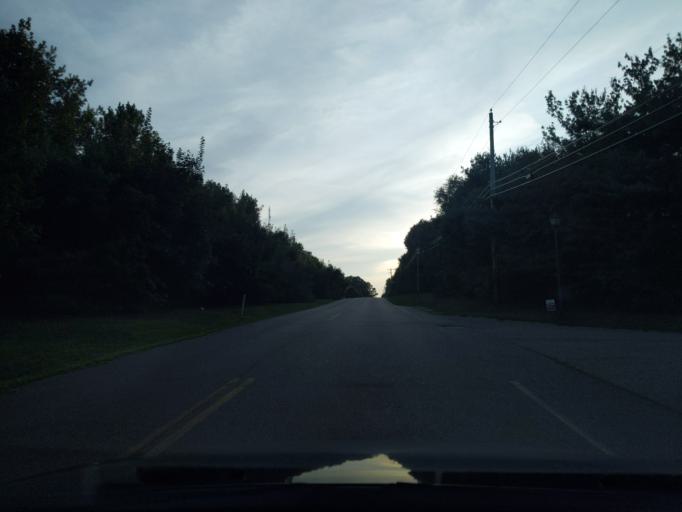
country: US
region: Ohio
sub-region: Stark County
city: Greentown
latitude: 40.9145
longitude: -81.3926
